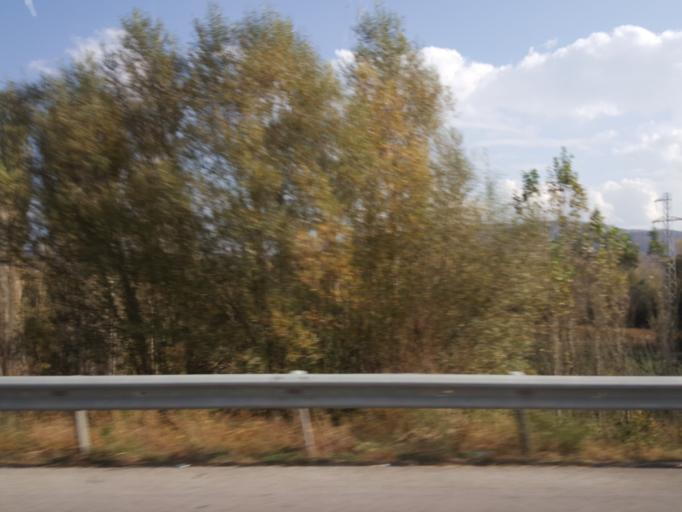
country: TR
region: Corum
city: Seydim
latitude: 40.4070
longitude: 34.7270
